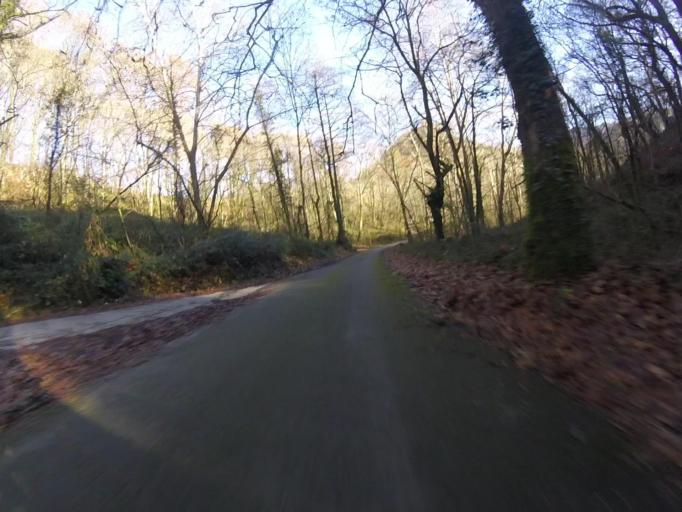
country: ES
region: Navarre
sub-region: Provincia de Navarra
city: Bera
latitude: 43.2878
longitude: -1.6440
